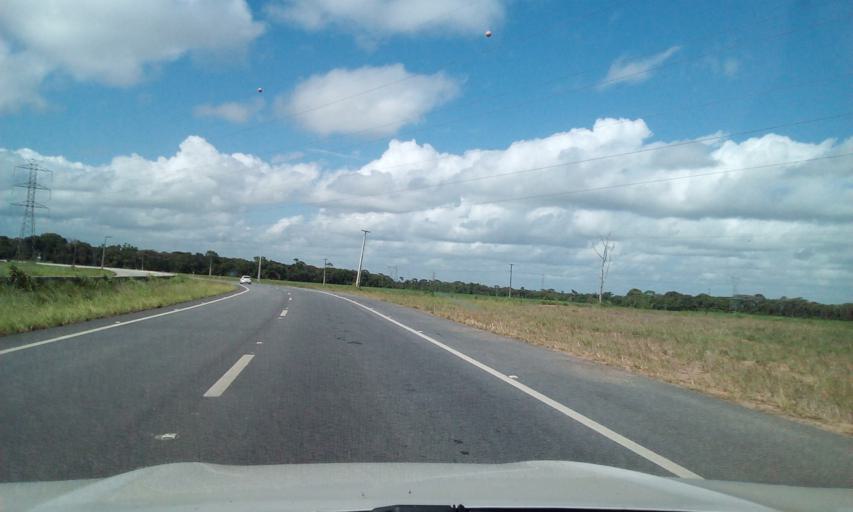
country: BR
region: Alagoas
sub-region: Rio Largo
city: Rio Largo
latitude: -9.4406
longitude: -35.8366
